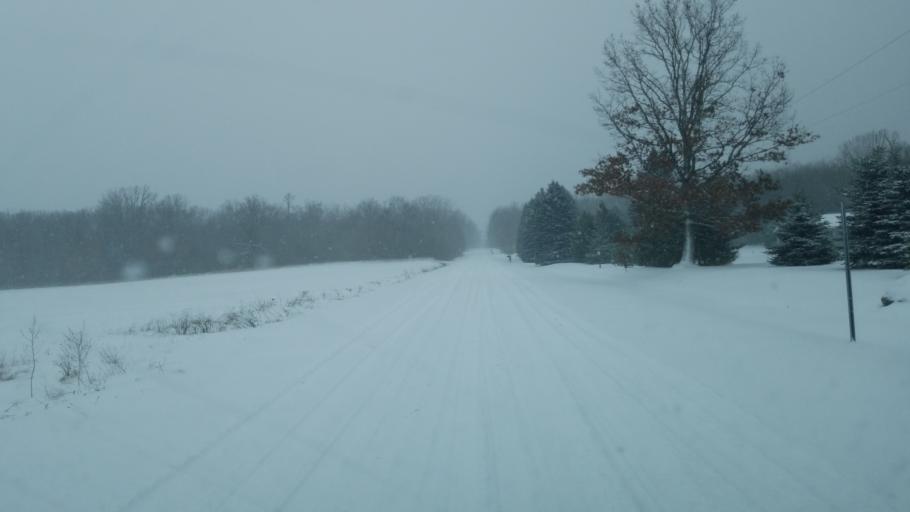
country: US
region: Michigan
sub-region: Mecosta County
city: Canadian Lakes
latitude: 43.5763
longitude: -85.3443
